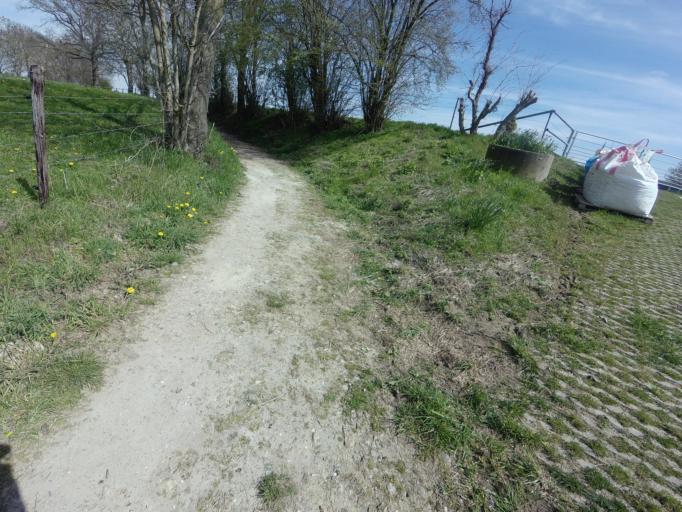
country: NL
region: Limburg
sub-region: Eijsden-Margraten
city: Margraten
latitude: 50.7885
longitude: 5.8176
